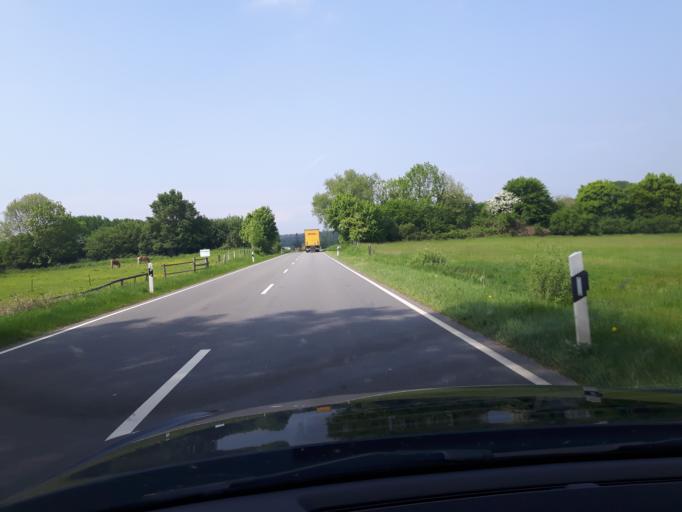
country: DE
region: Mecklenburg-Vorpommern
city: Selmsdorf
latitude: 53.8785
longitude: 10.8684
